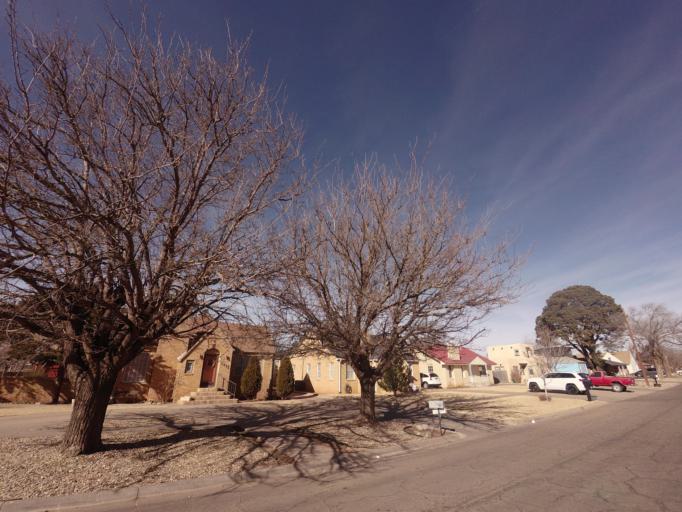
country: US
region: New Mexico
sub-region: Curry County
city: Clovis
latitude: 34.4126
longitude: -103.2015
